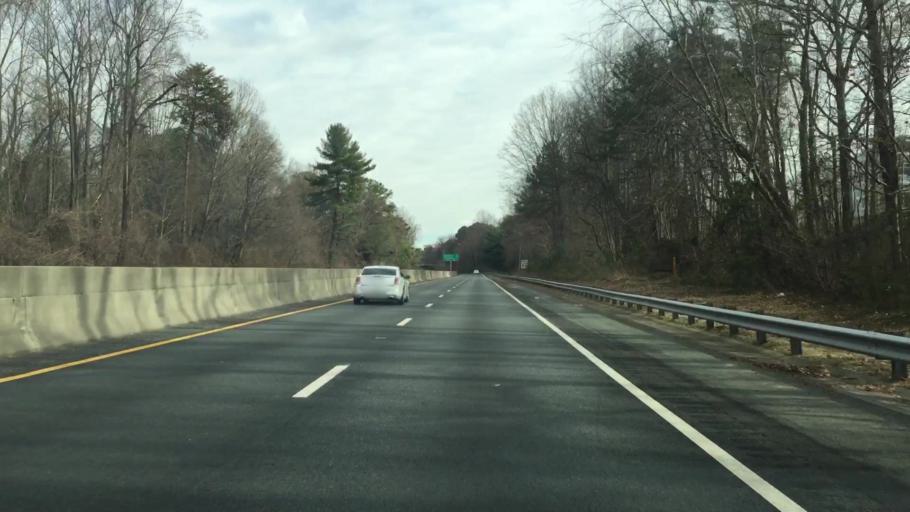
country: US
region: North Carolina
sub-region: Forsyth County
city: Winston-Salem
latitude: 36.0886
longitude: -80.2959
